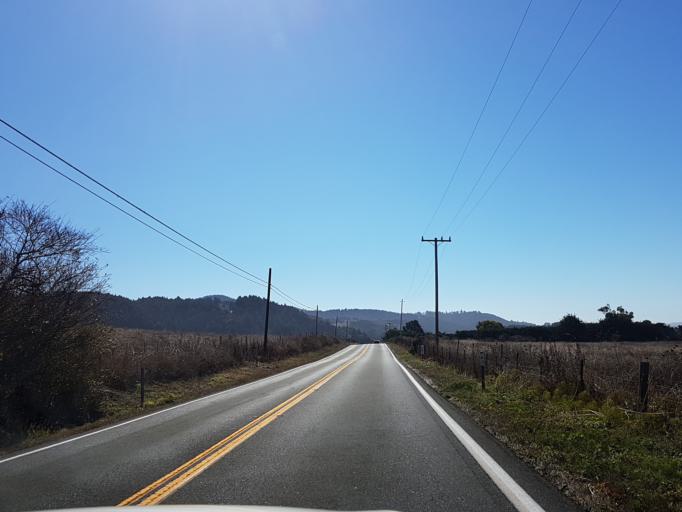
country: US
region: California
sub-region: Mendocino County
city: Boonville
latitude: 39.0698
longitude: -123.6918
